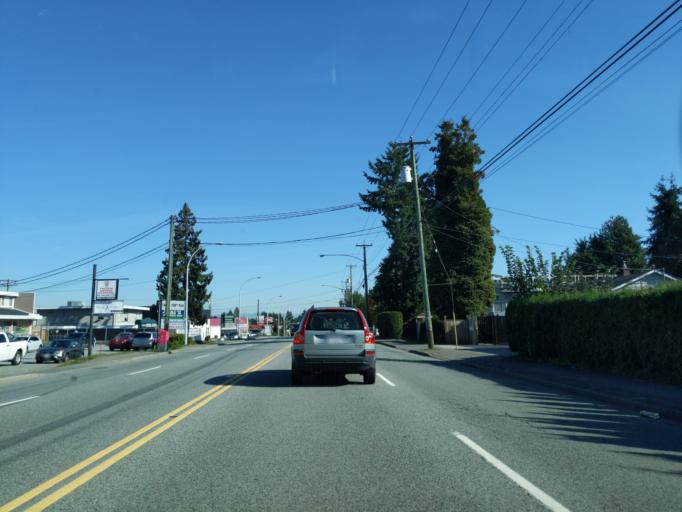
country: CA
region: British Columbia
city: Port Moody
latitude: 49.1987
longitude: -122.8162
